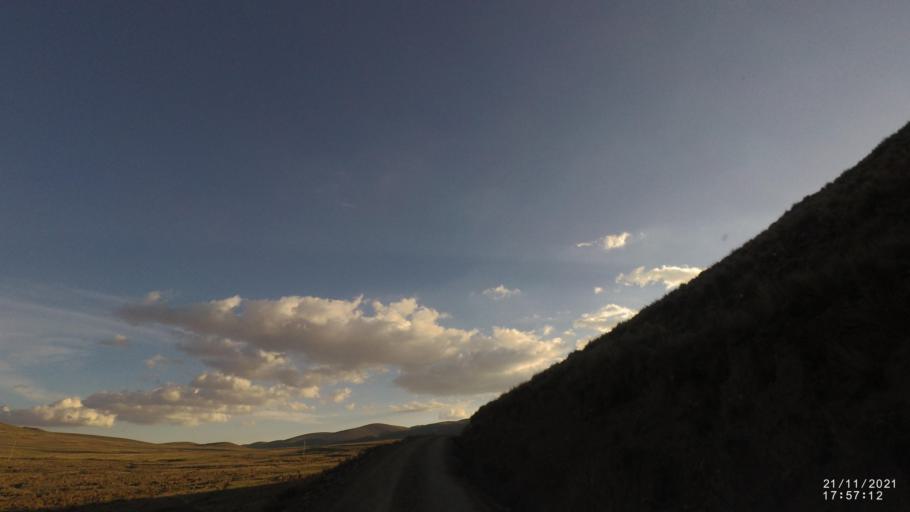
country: BO
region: Cochabamba
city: Cochabamba
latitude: -17.2267
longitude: -66.2320
